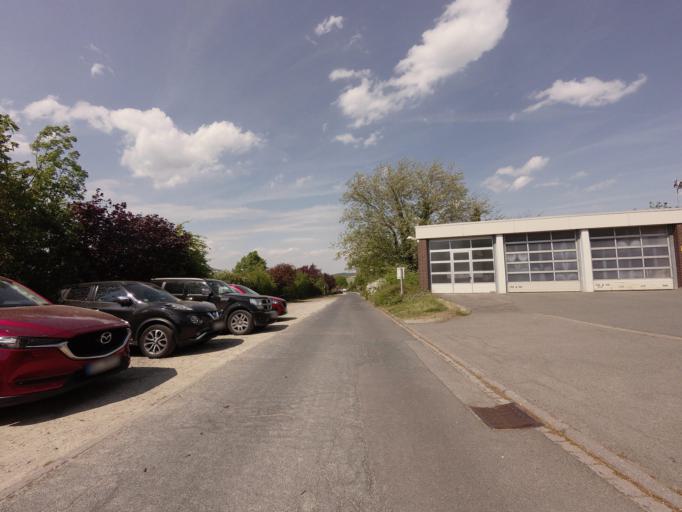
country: DE
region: Lower Saxony
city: Giesen
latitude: 52.1498
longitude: 9.8900
